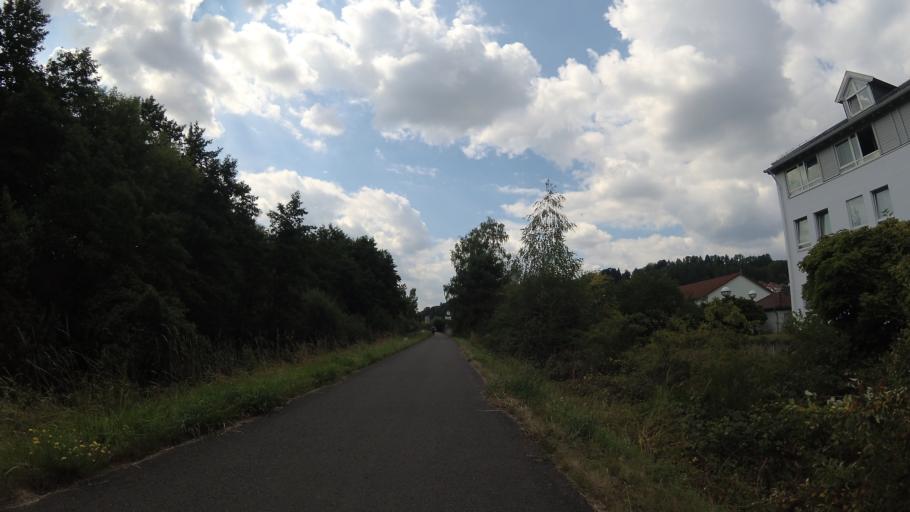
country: DE
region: Saarland
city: Blieskastel
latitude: 49.2349
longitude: 7.2602
